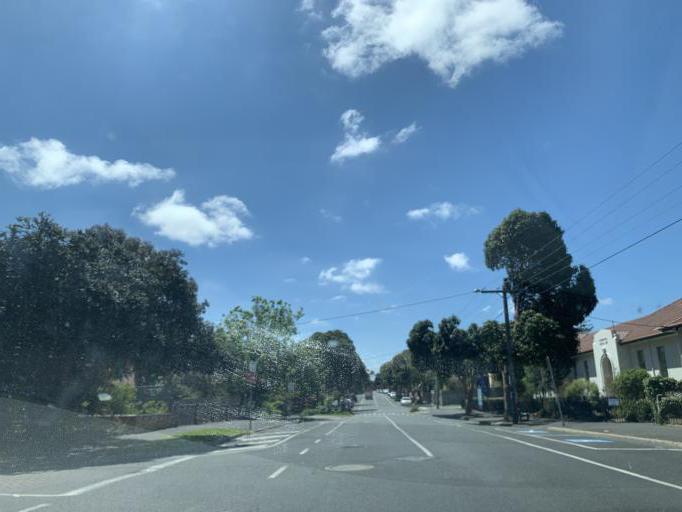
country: AU
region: Victoria
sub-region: Bayside
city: Brighton East
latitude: -37.9050
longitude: 145.0147
